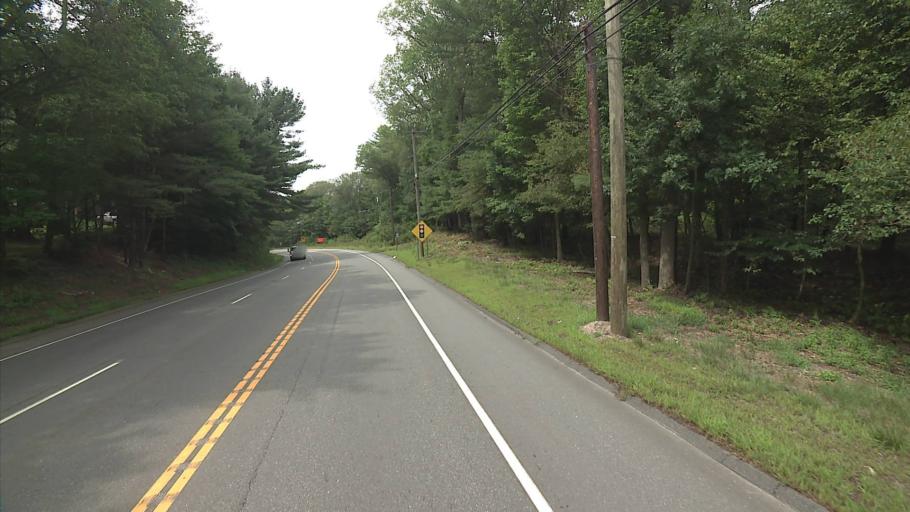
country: US
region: Connecticut
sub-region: Tolland County
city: Stafford Springs
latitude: 41.8822
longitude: -72.2939
